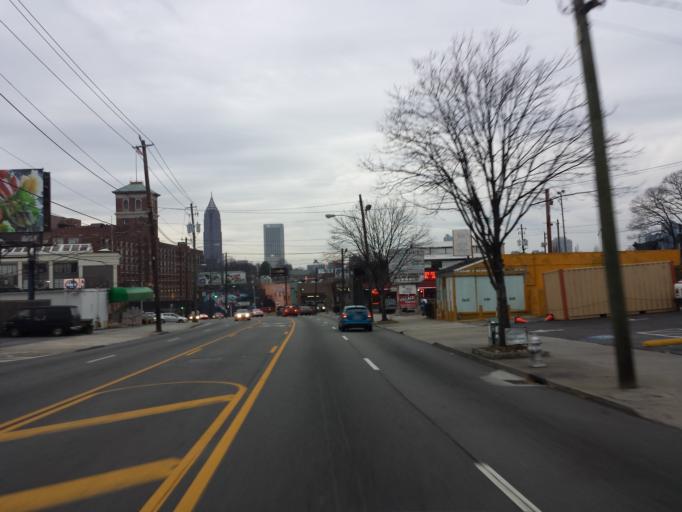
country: US
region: Georgia
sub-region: DeKalb County
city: Druid Hills
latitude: 33.7738
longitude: -84.3622
